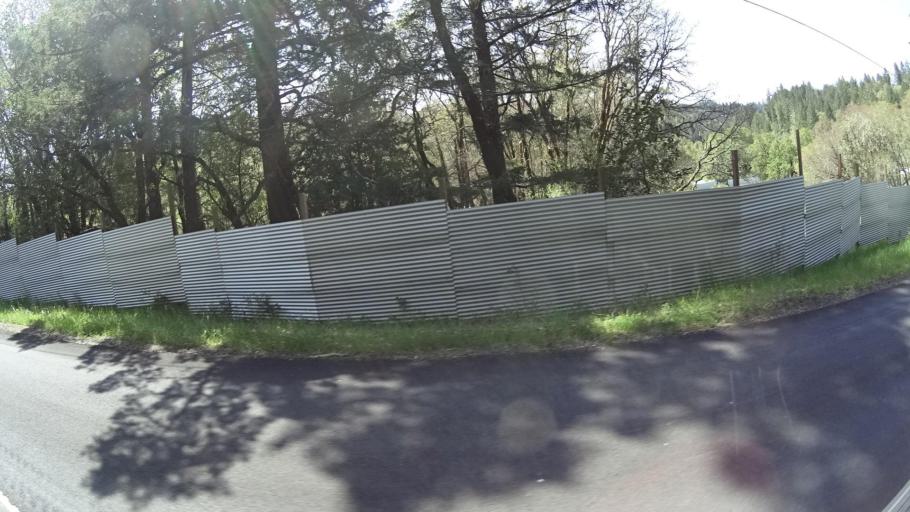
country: US
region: California
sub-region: Humboldt County
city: Redway
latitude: 40.3072
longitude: -123.6547
